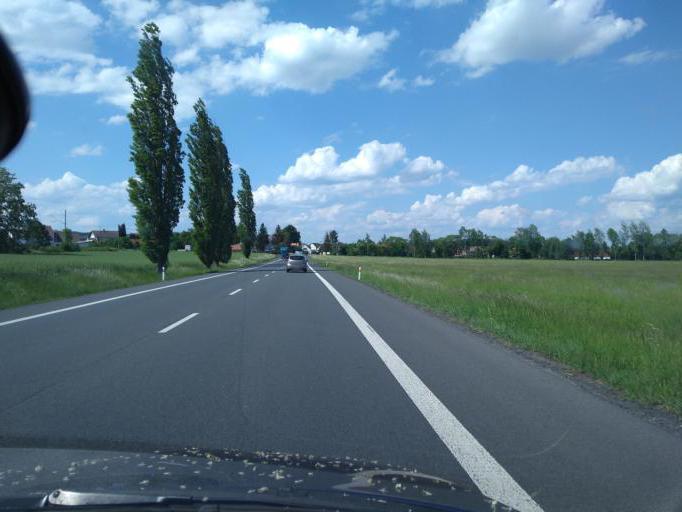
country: CZ
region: Plzensky
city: Svihov
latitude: 49.5206
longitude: 13.3010
